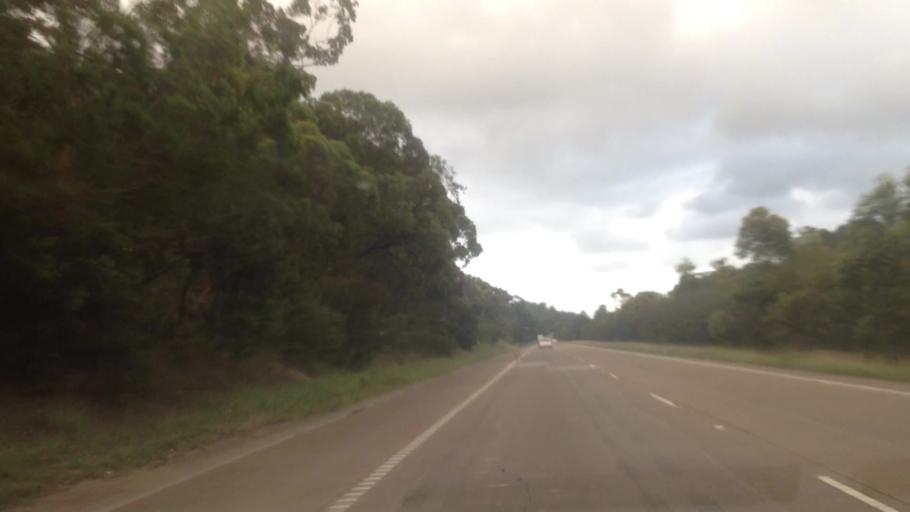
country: AU
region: New South Wales
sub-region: Wyong Shire
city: Charmhaven
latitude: -33.1636
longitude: 151.4687
